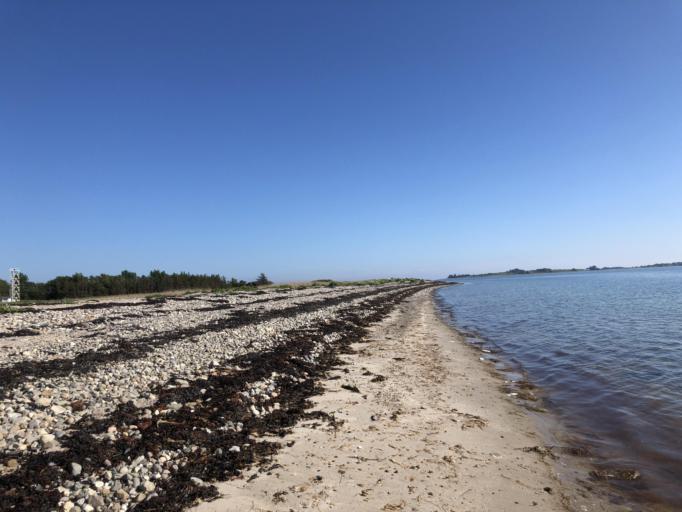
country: DK
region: Zealand
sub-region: Slagelse Kommune
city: Skaelskor
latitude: 55.2005
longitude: 11.1740
